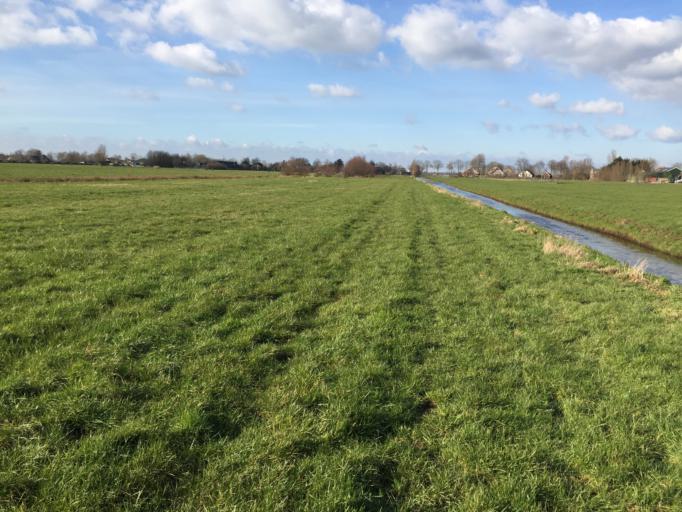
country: NL
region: Utrecht
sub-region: Gemeente Lopik
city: Lopik
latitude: 51.9949
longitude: 4.9250
